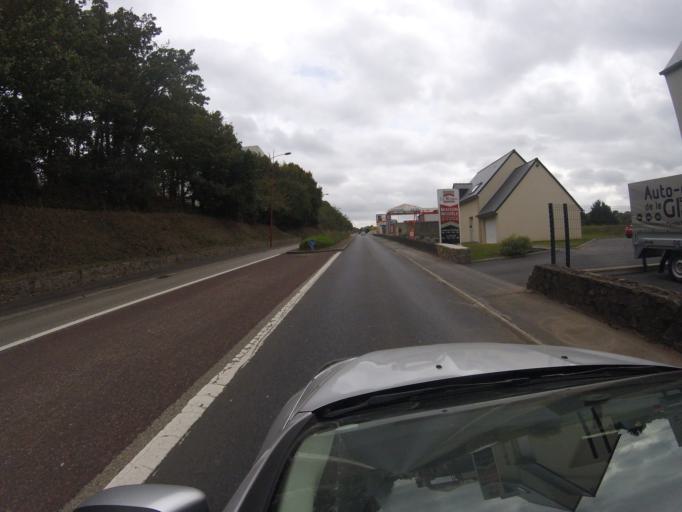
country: FR
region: Lower Normandy
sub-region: Departement de la Manche
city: Cherbourg-Octeville
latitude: 49.6179
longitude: -1.6096
